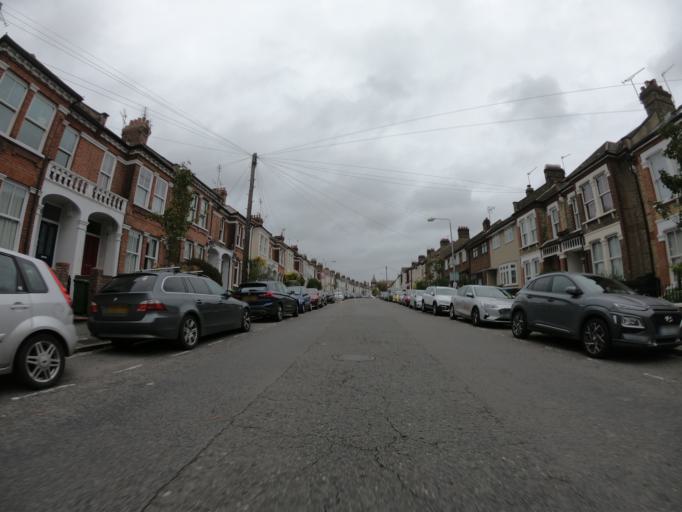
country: GB
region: England
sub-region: Greater London
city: Blackheath
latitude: 51.4831
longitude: 0.0239
